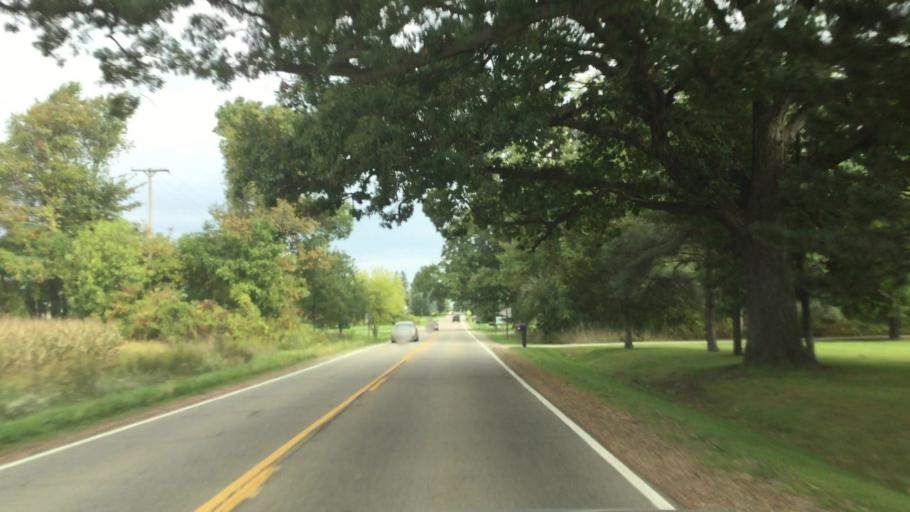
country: US
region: Michigan
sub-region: Livingston County
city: Howell
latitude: 42.6808
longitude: -83.8775
